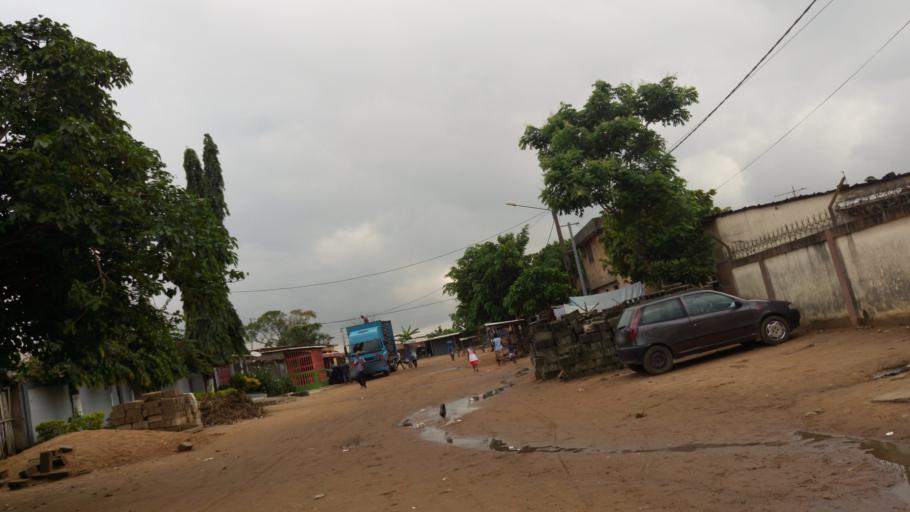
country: CI
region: Lagunes
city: Abobo
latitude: 5.4090
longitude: -3.9972
